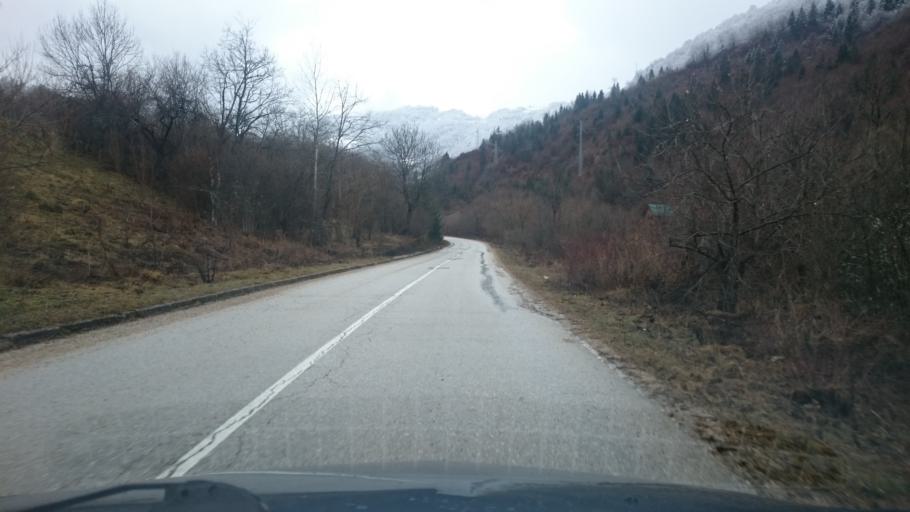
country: BA
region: Republika Srpska
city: Skender Vakuf
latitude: 44.4298
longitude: 17.4030
